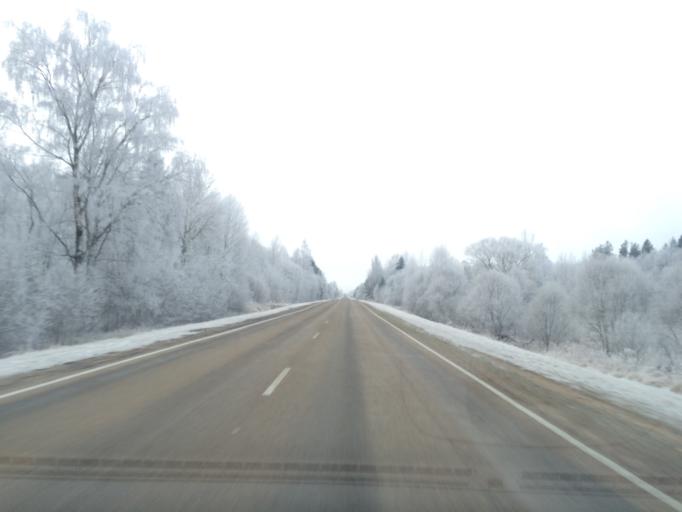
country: LV
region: Rezekne
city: Rezekne
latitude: 56.6478
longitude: 27.4922
